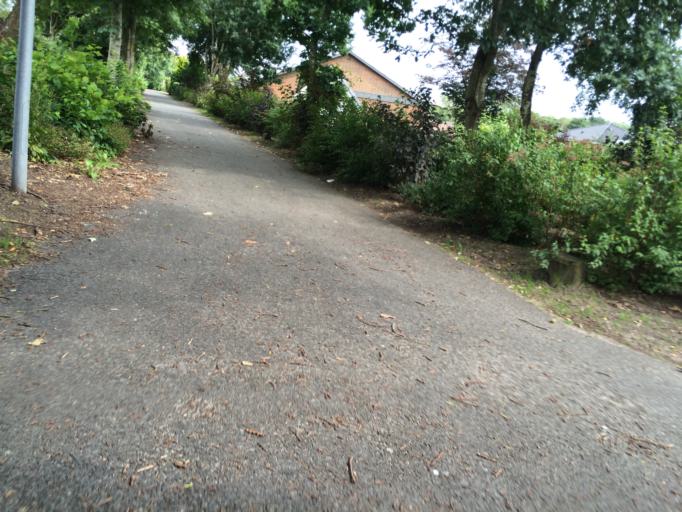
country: DK
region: Central Jutland
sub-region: Holstebro Kommune
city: Ulfborg
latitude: 56.2724
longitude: 8.3086
